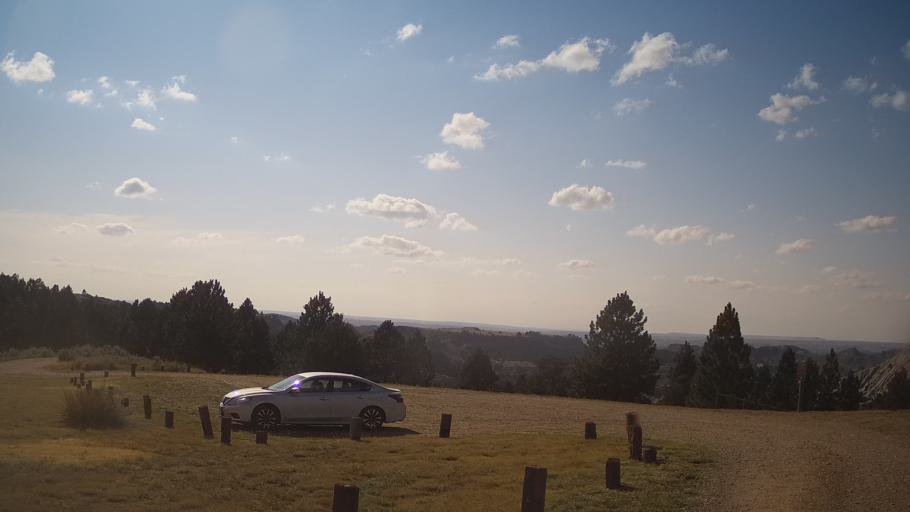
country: US
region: Montana
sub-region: Dawson County
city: Glendive
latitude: 47.0630
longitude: -104.6728
